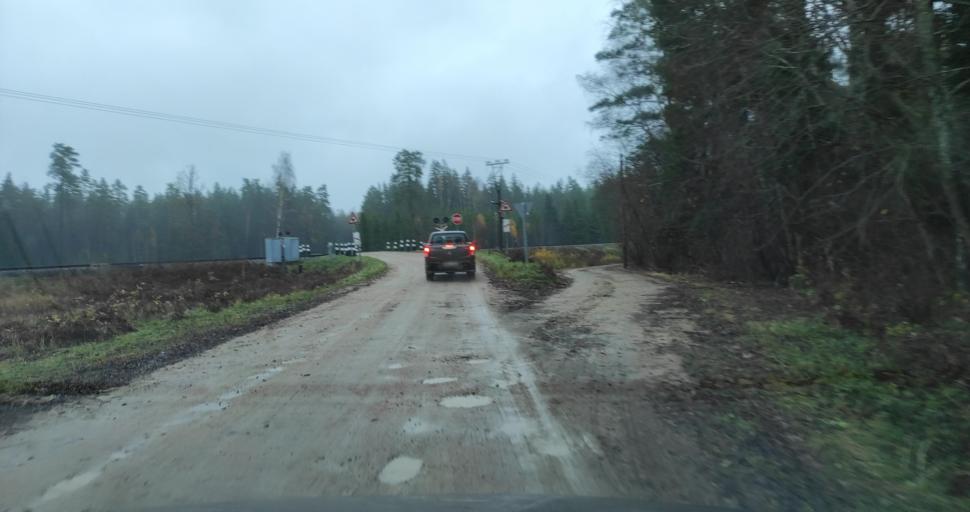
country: LV
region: Skrunda
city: Skrunda
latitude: 56.6895
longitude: 22.0795
